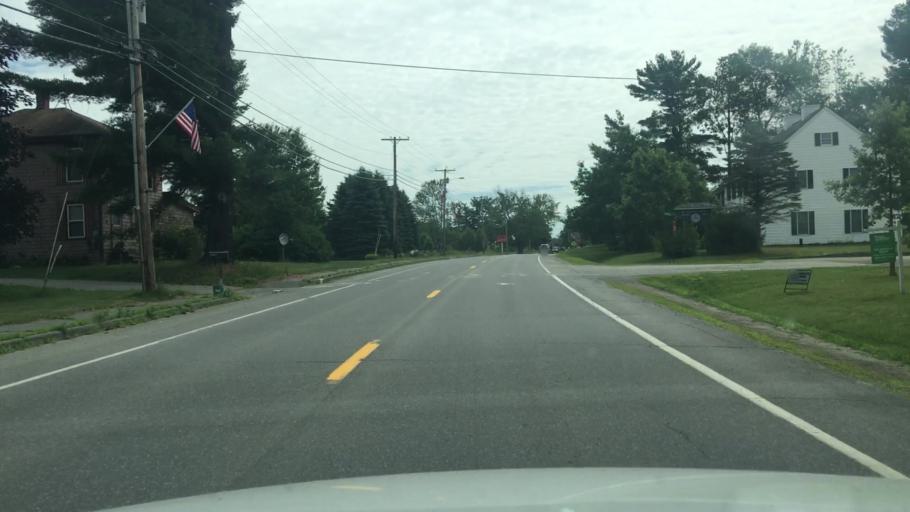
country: US
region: Maine
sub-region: Waldo County
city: Troy
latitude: 44.6127
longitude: -69.3440
